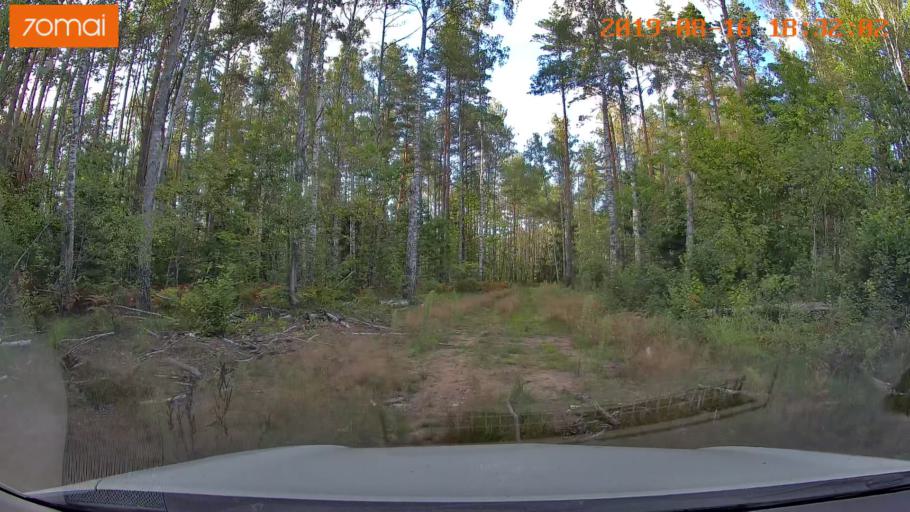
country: BY
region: Mogilev
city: Asipovichy
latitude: 53.1987
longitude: 28.6392
